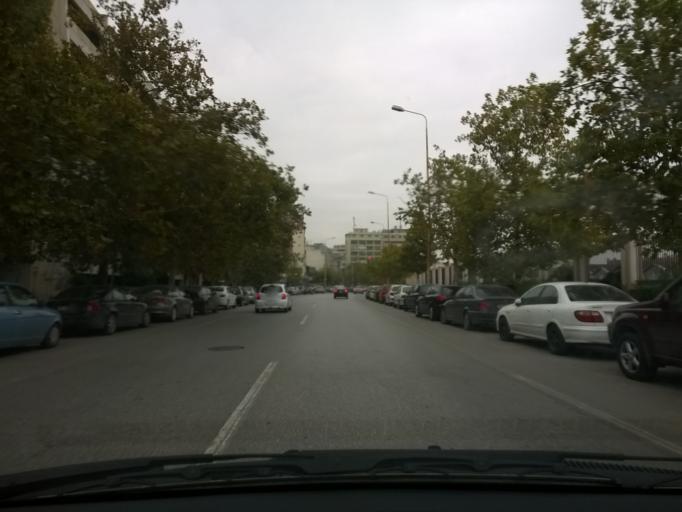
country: GR
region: Central Macedonia
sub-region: Nomos Thessalonikis
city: Thessaloniki
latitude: 40.6374
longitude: 22.9334
